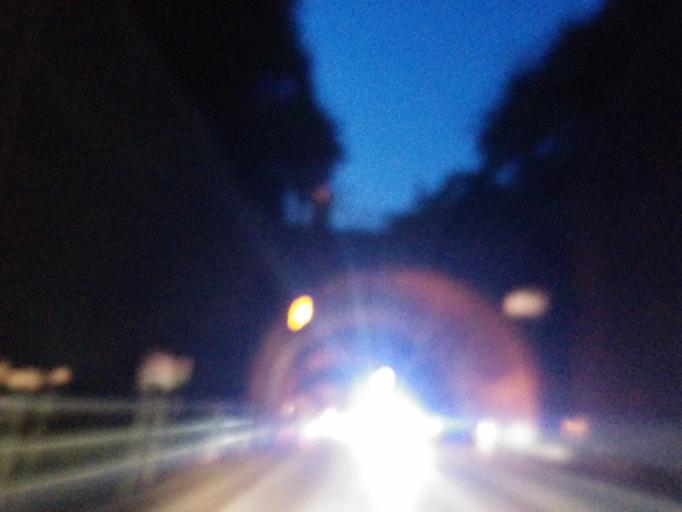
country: JP
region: Gifu
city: Mino
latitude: 35.6254
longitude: 136.9471
